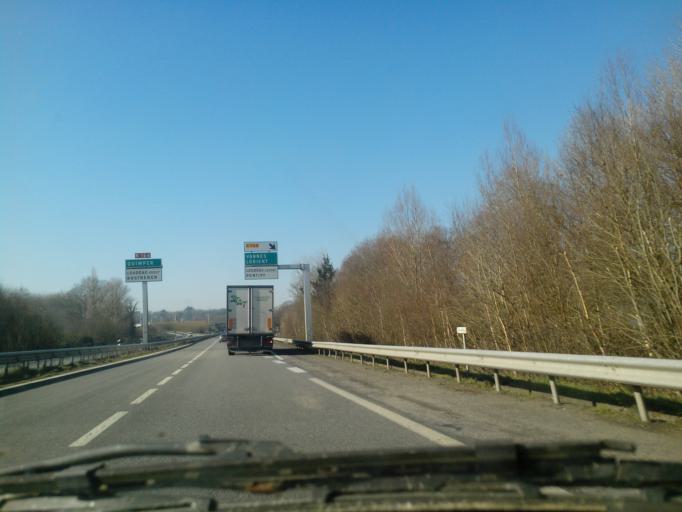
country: FR
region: Brittany
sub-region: Departement des Cotes-d'Armor
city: Loudeac
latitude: 48.1800
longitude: -2.7245
